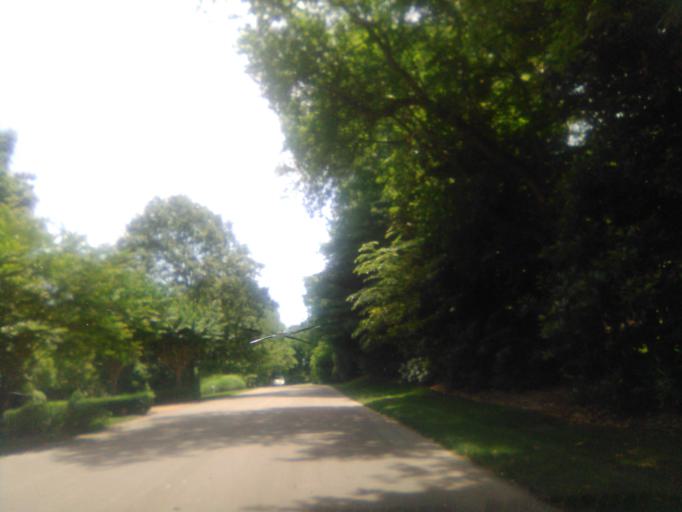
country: US
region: Tennessee
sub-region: Davidson County
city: Belle Meade
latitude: 36.1189
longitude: -86.8464
